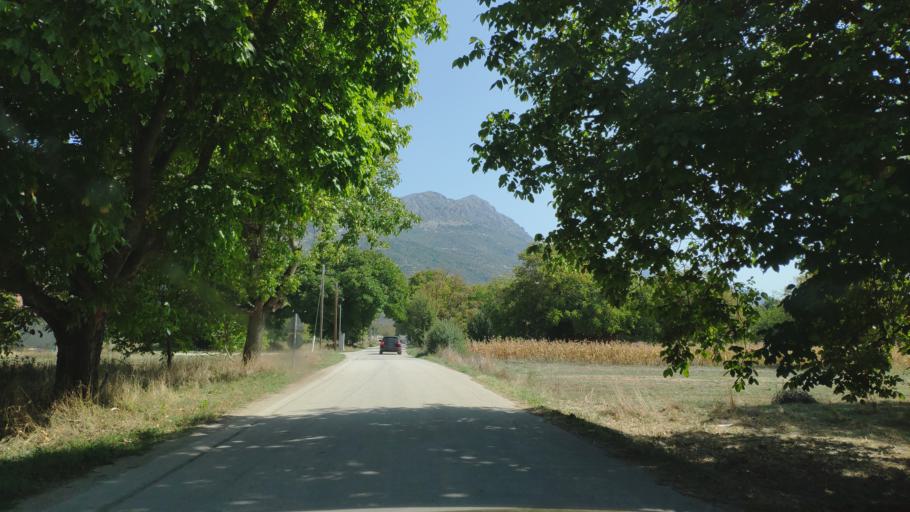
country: GR
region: West Greece
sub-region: Nomos Achaias
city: Kalavryta
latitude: 37.9090
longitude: 22.3160
